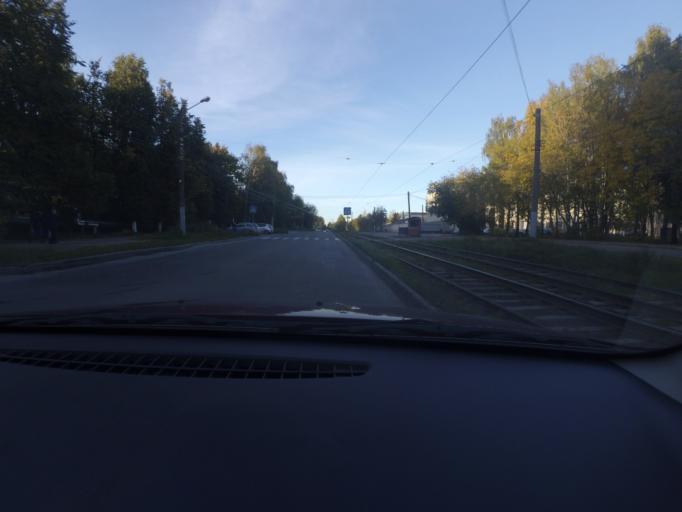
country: RU
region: Nizjnij Novgorod
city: Nizhniy Novgorod
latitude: 56.2819
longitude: 43.9931
